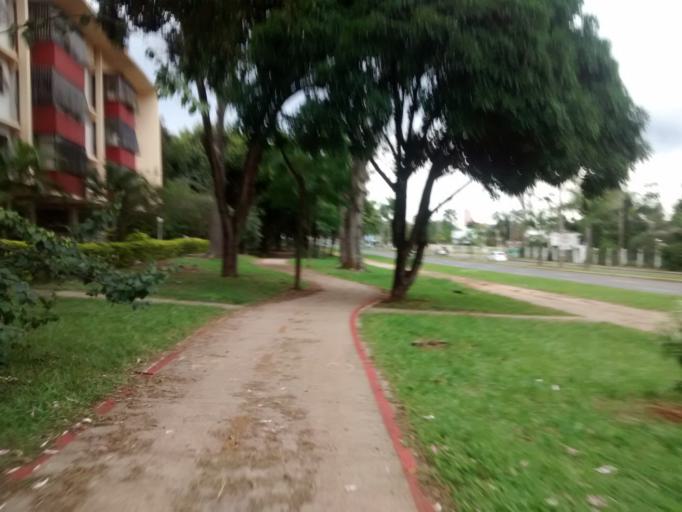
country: BR
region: Federal District
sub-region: Brasilia
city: Brasilia
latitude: -15.7640
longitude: -47.8769
